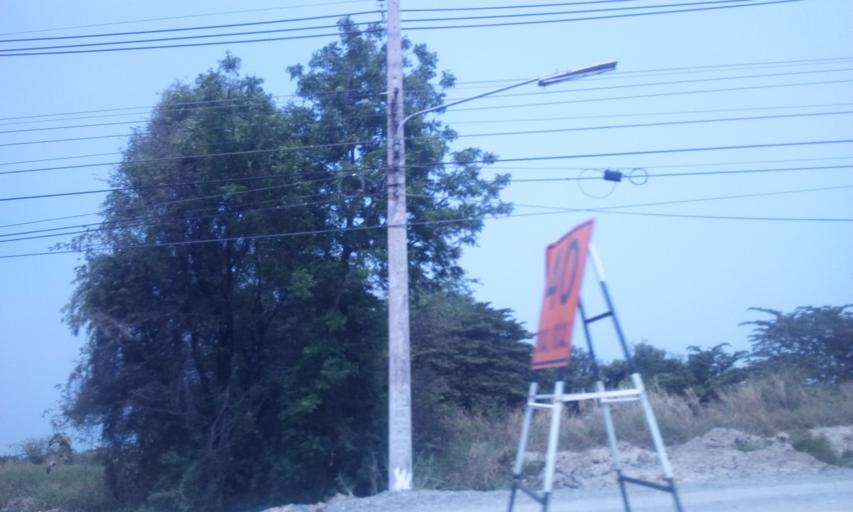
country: TH
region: Chachoengsao
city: Ban Pho
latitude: 13.5531
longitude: 101.1393
